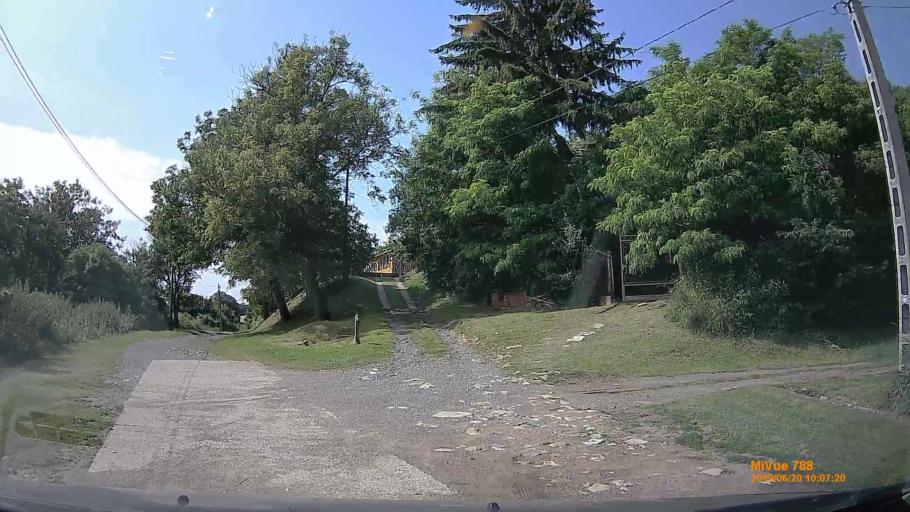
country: HU
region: Baranya
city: Mecseknadasd
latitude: 46.1826
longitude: 18.4794
